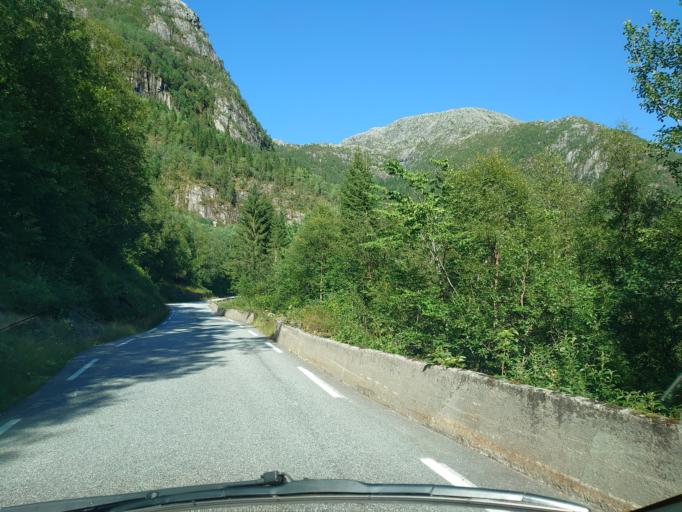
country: NO
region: Hordaland
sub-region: Vaksdal
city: Dale
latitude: 60.5868
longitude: 5.8413
